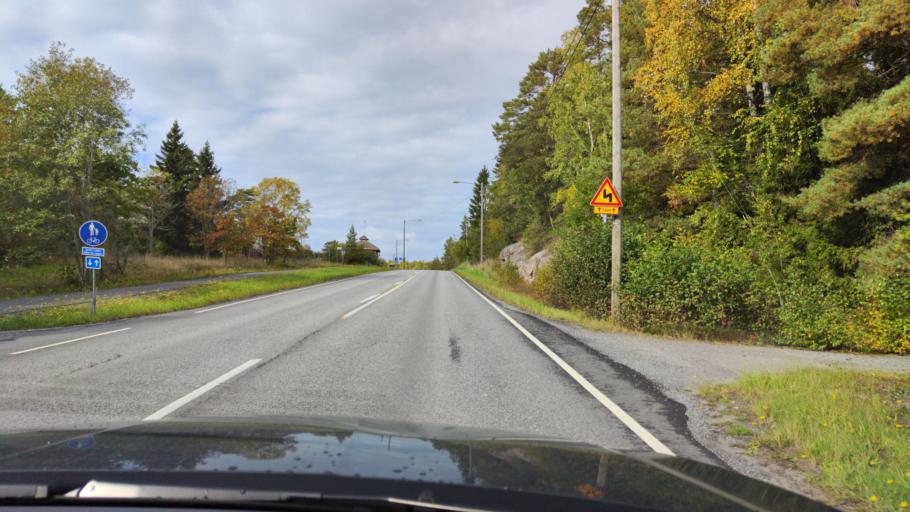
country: FI
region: Varsinais-Suomi
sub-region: Turku
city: Raisio
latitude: 60.3656
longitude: 22.1774
